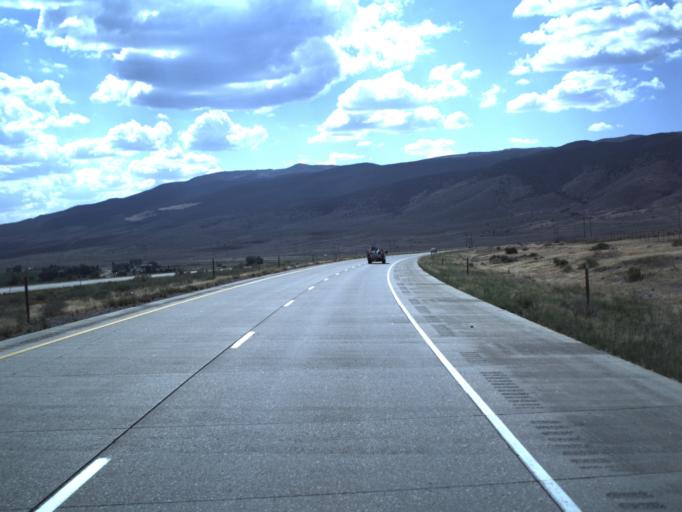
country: US
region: Utah
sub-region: Sevier County
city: Monroe
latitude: 38.6592
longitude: -112.1853
